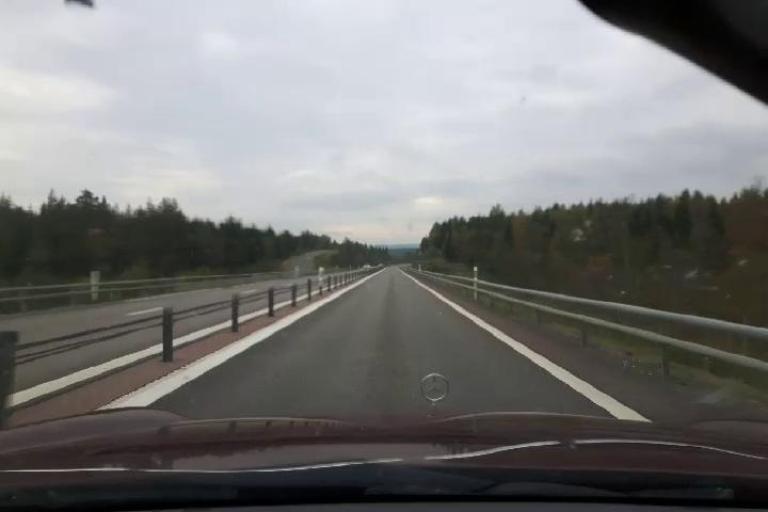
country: SE
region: Vaesternorrland
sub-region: Haernoesands Kommun
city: Haernoesand
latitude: 62.7137
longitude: 17.9036
